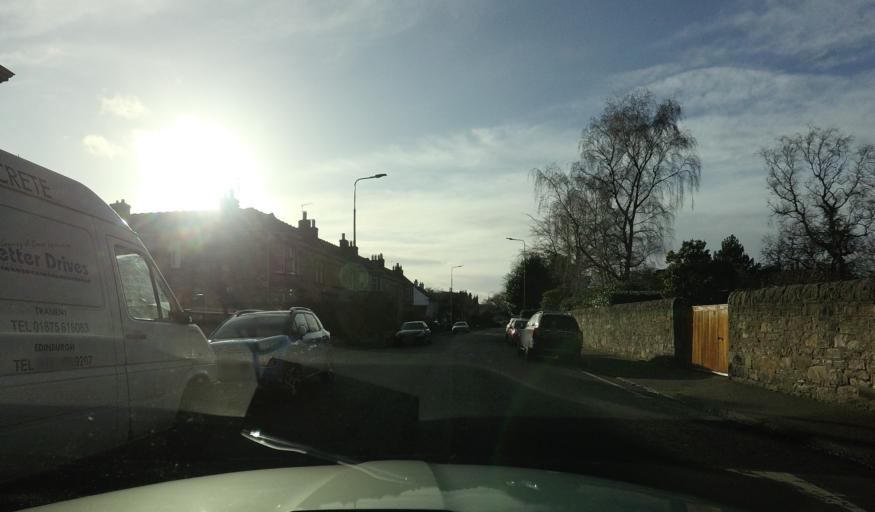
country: GB
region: Scotland
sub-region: Edinburgh
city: Edinburgh
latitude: 55.9766
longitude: -3.2009
